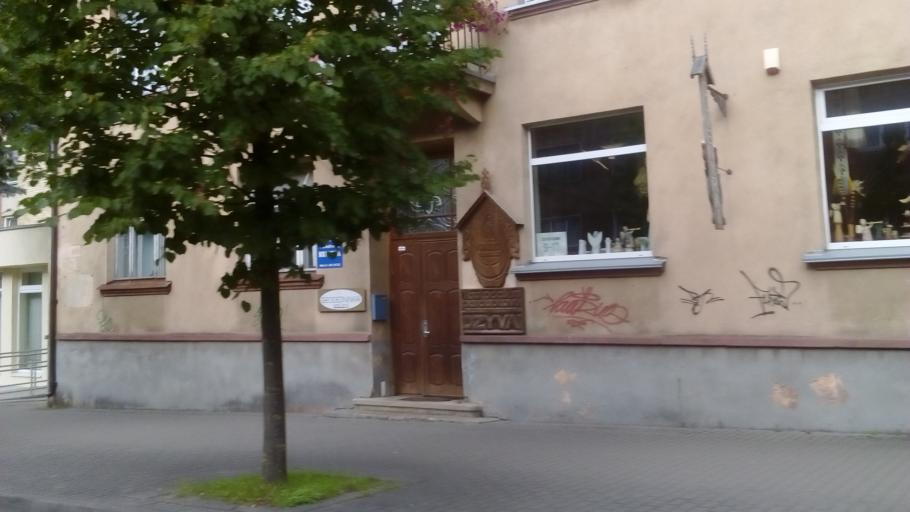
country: LT
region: Alytaus apskritis
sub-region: Alytus
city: Alytus
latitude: 54.3979
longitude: 24.0485
